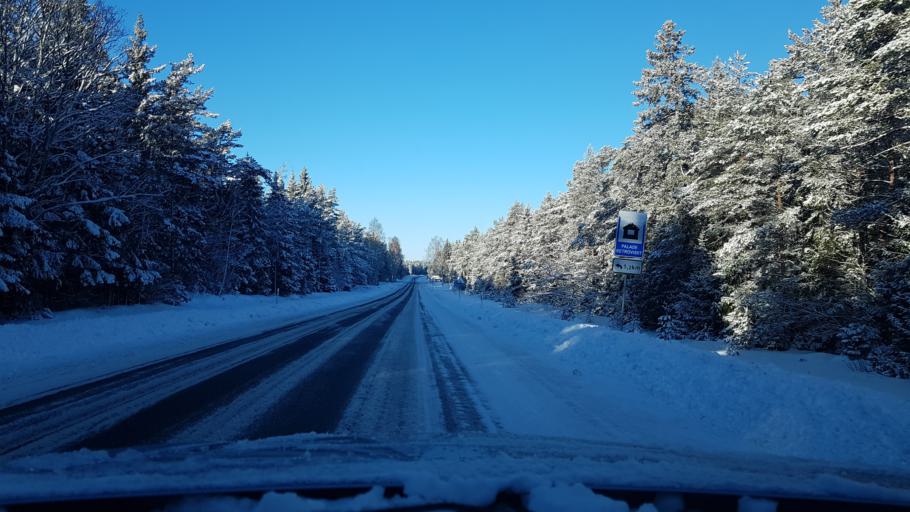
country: EE
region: Hiiumaa
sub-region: Kaerdla linn
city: Kardla
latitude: 58.9612
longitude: 22.8485
